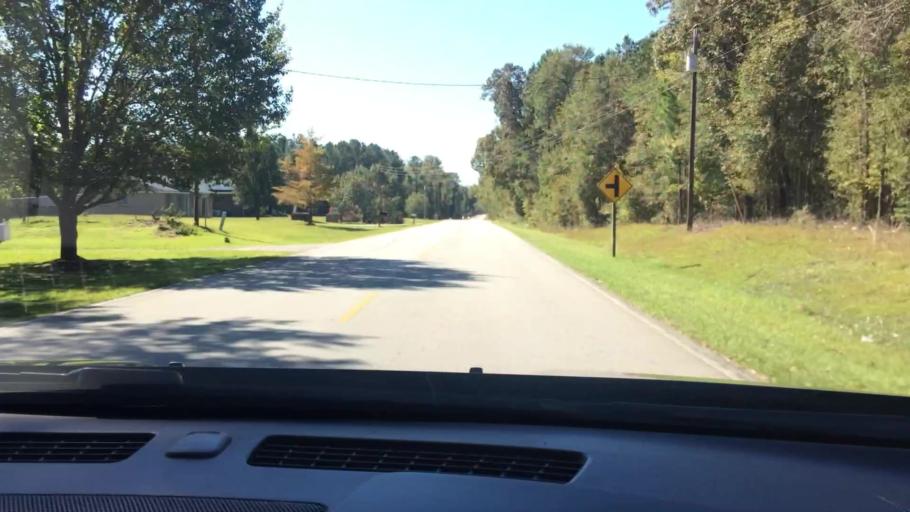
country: US
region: North Carolina
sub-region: Craven County
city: Vanceboro
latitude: 35.3200
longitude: -77.2938
